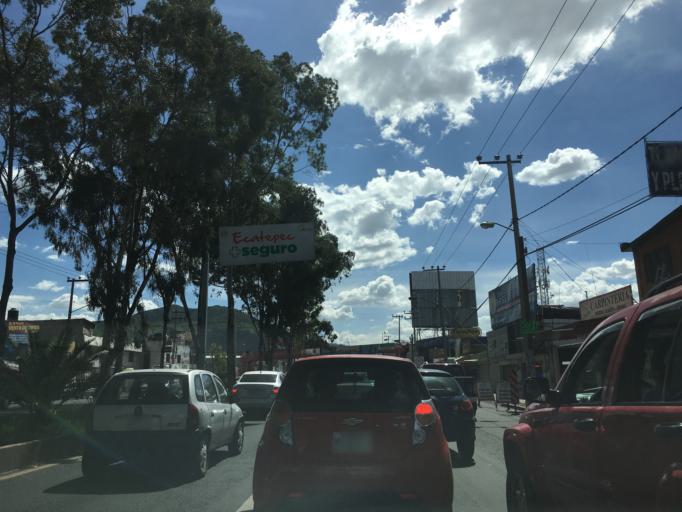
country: MX
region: Mexico
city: Ecatepec
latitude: 19.6135
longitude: -99.0469
